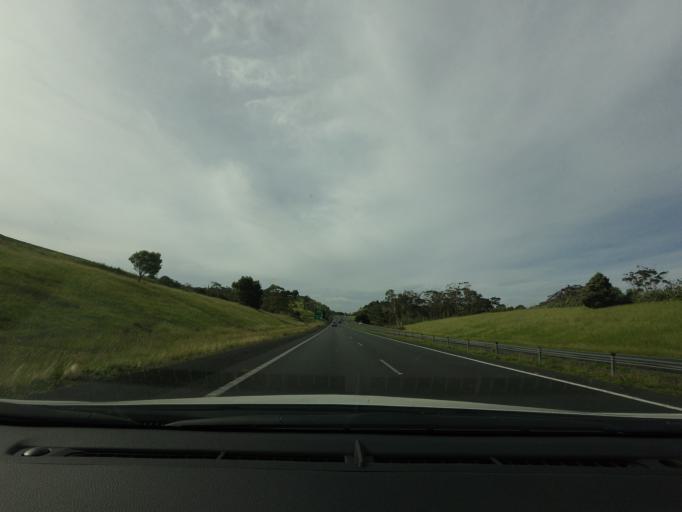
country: NZ
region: Auckland
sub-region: Auckland
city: Rothesay Bay
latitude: -36.6009
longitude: 174.6623
